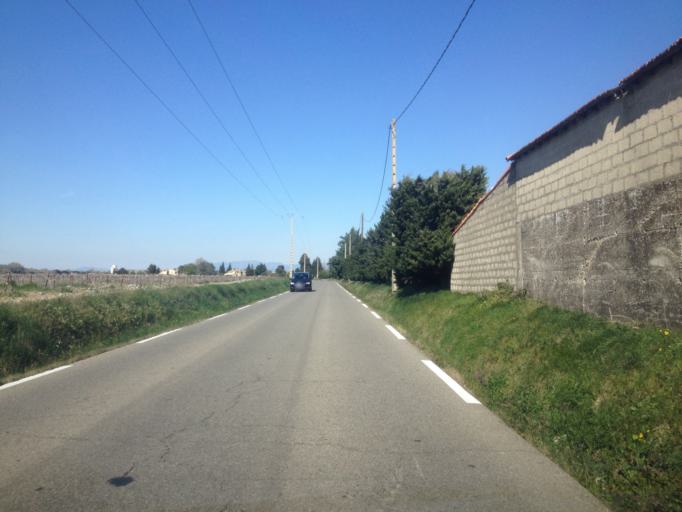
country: FR
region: Provence-Alpes-Cote d'Azur
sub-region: Departement du Vaucluse
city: Serignan-du-Comtat
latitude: 44.1613
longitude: 4.8300
